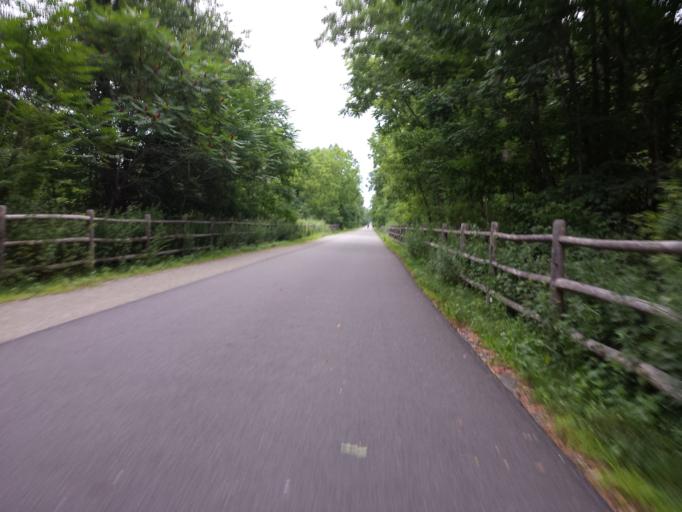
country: US
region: New York
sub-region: Dutchess County
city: Red Oaks Mill
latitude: 41.6464
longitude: -73.8593
